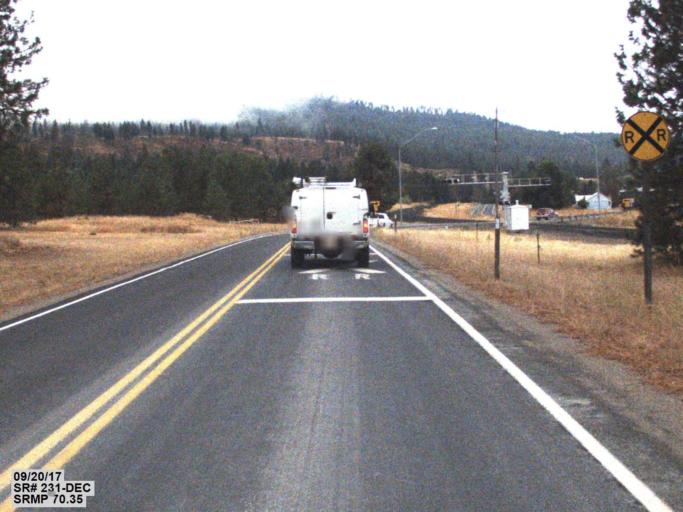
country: US
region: Washington
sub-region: Stevens County
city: Chewelah
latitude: 48.1551
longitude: -117.7257
